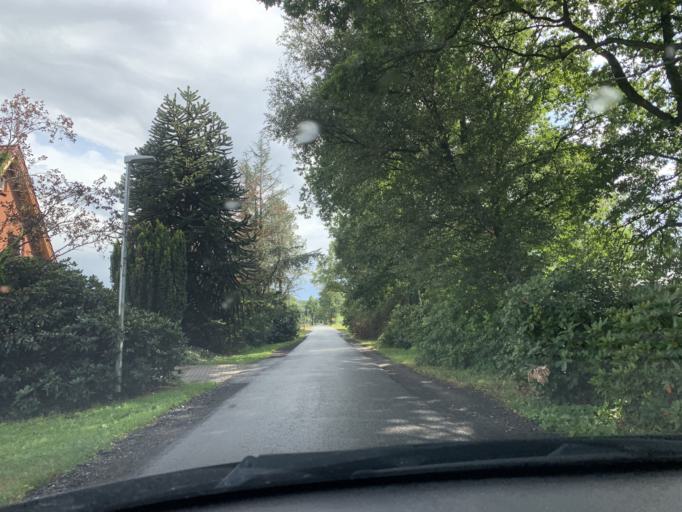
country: DE
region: Lower Saxony
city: Westerstede
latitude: 53.2584
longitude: 7.9015
